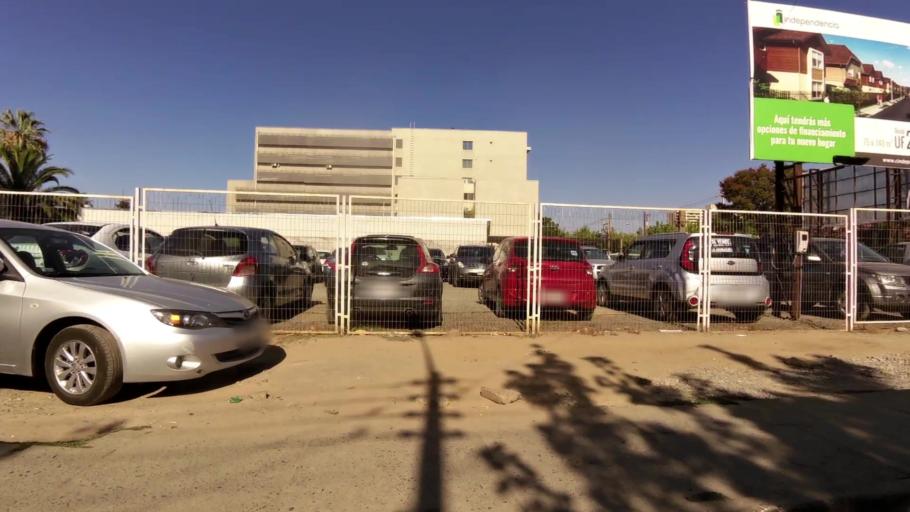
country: CL
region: Maule
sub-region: Provincia de Talca
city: Talca
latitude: -35.4260
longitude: -71.6625
